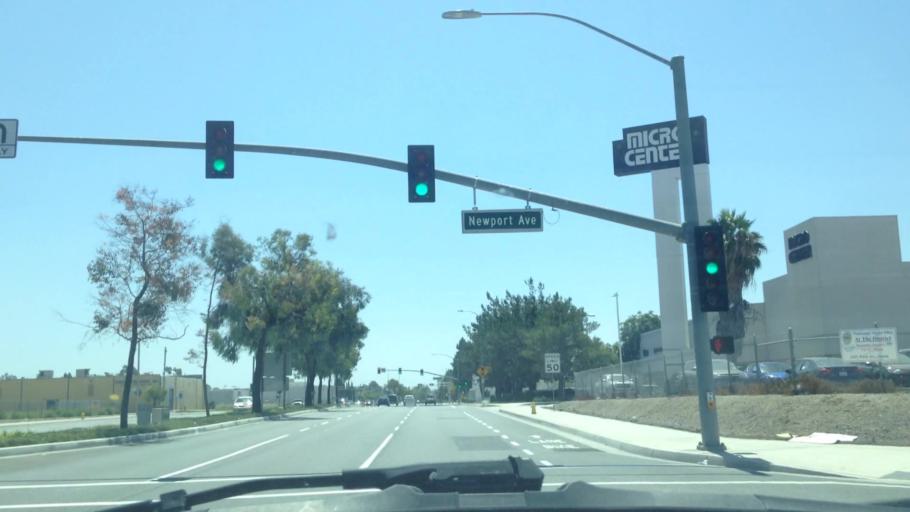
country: US
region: California
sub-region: Orange County
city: Tustin
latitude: 33.7256
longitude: -117.8333
